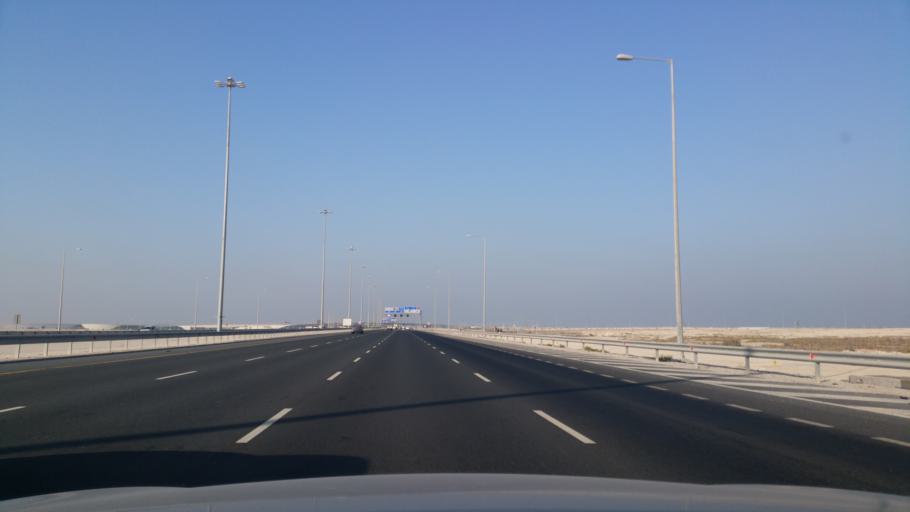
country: QA
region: Al Wakrah
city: Al Wukayr
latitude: 25.1094
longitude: 51.5834
